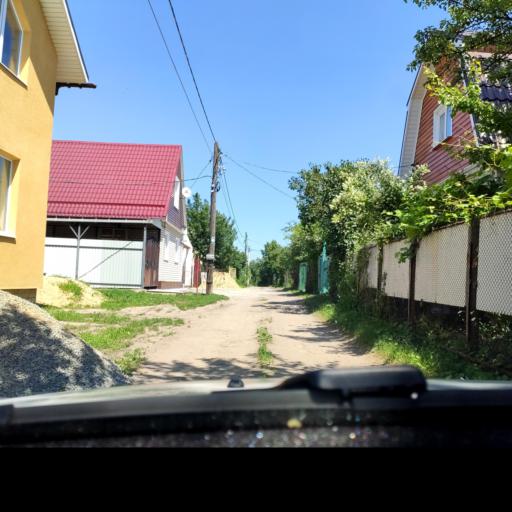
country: RU
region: Voronezj
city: Shilovo
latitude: 51.5897
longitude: 39.1492
